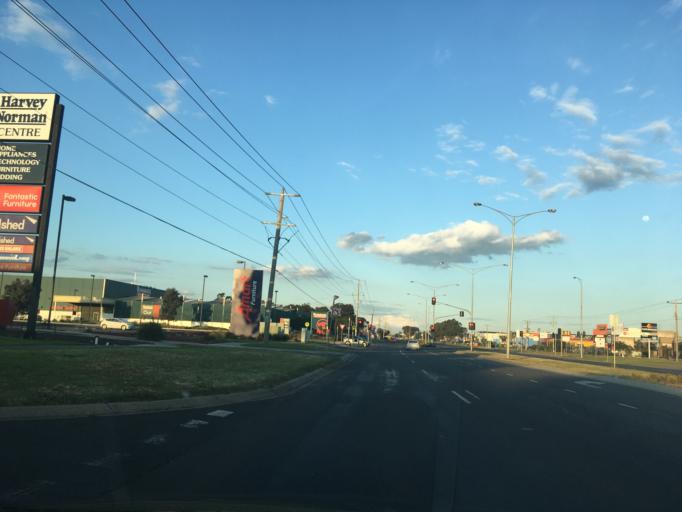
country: AU
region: Victoria
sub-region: Wyndham
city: Hoppers Crossing
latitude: -37.8771
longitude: 144.7125
